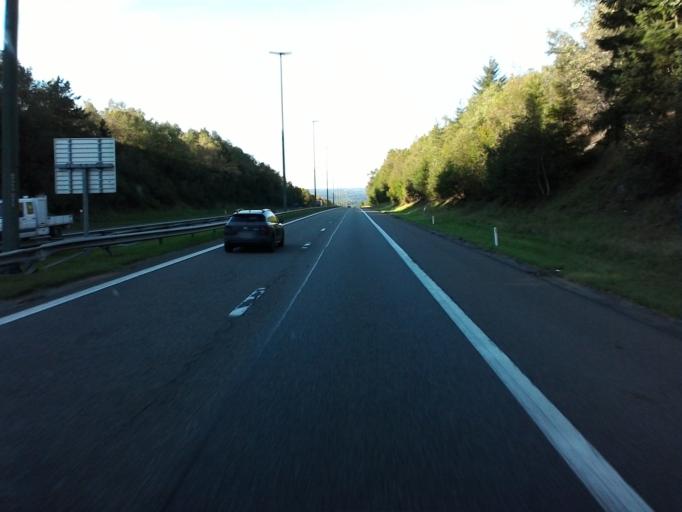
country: BE
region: Wallonia
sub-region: Province du Luxembourg
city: Houffalize
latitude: 50.1091
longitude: 5.7582
